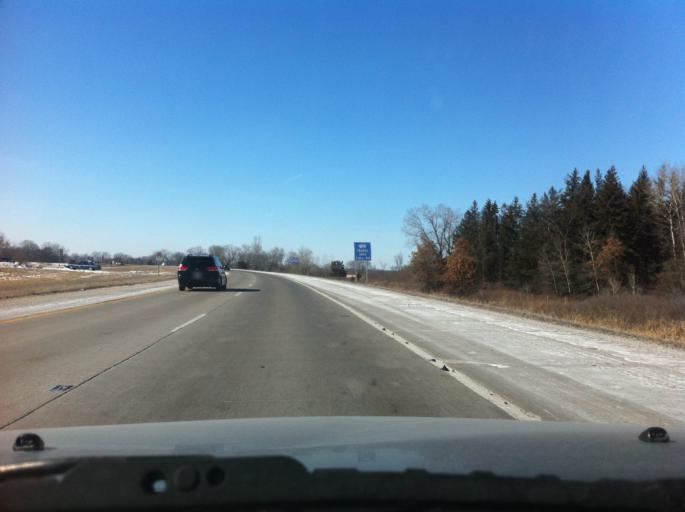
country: US
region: Wisconsin
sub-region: Columbia County
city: Portage
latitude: 43.4911
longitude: -89.4946
